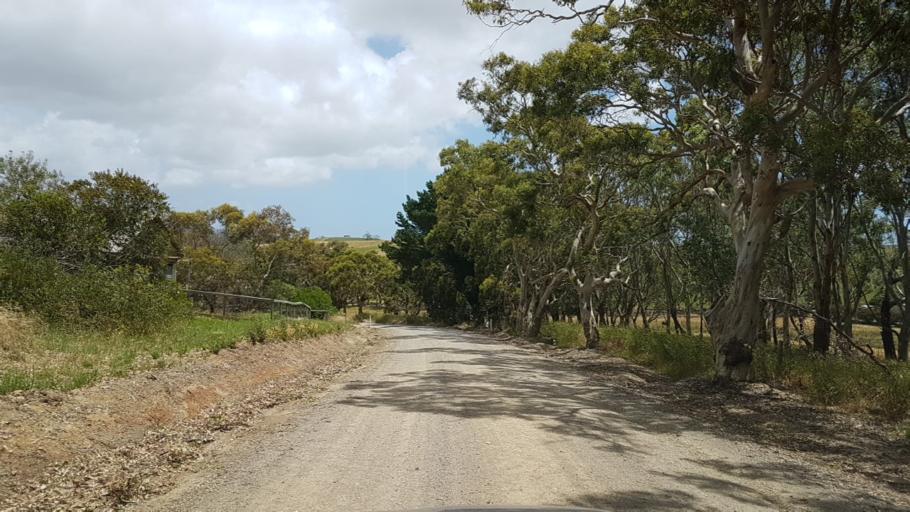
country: AU
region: South Australia
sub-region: Onkaparinga
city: Aldinga
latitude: -35.3653
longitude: 138.5242
